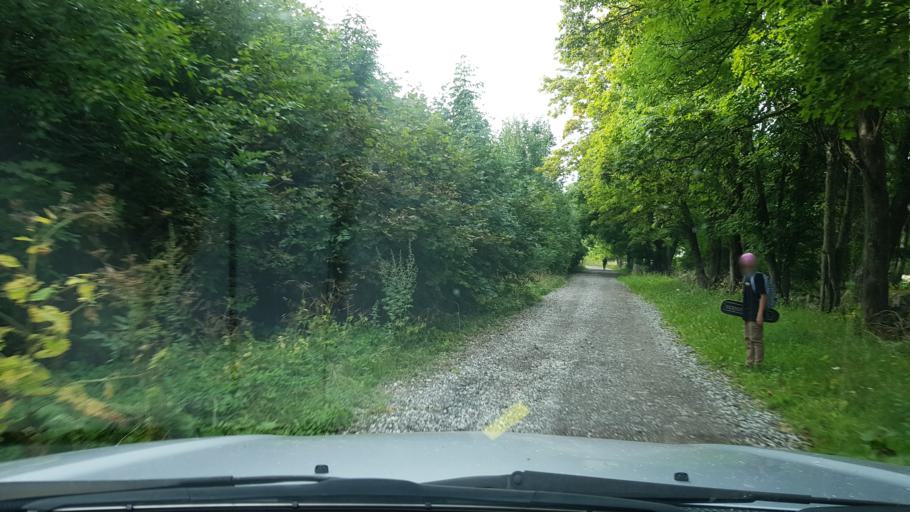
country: EE
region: Harju
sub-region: Rae vald
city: Jueri
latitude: 59.3611
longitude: 24.9174
